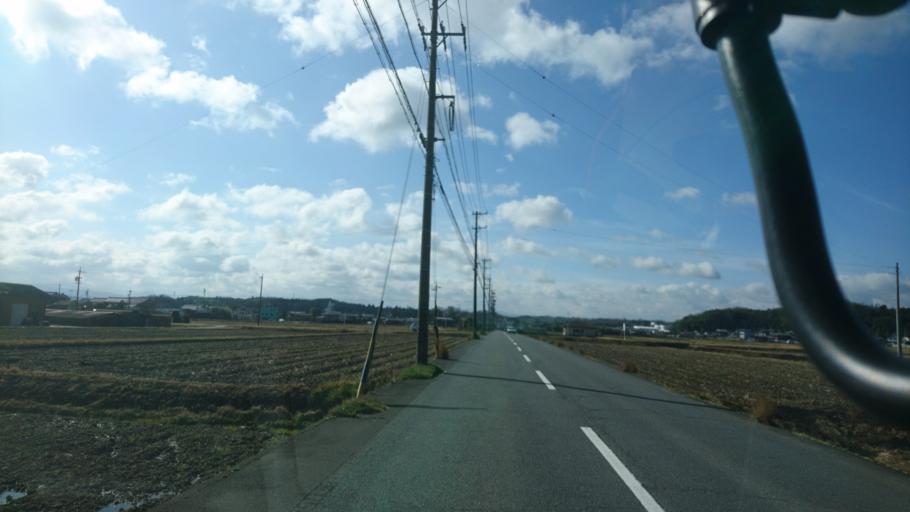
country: JP
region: Mie
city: Ueno-ebisumachi
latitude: 34.7472
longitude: 136.1100
